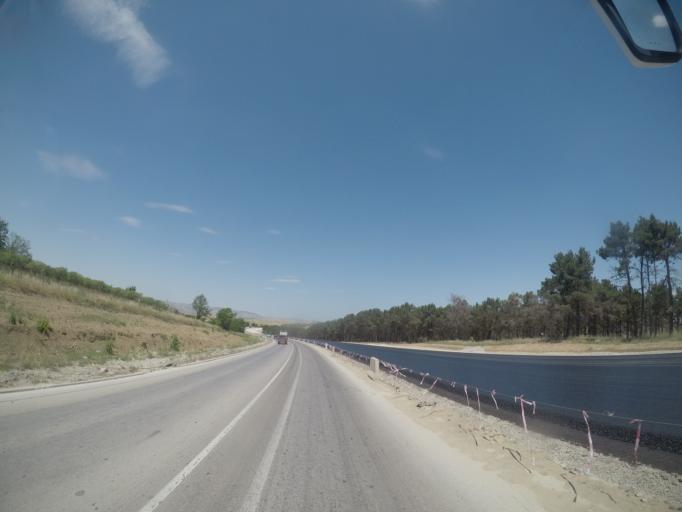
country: AZ
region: Qobustan
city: Qobustan
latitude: 40.5274
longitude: 48.7978
